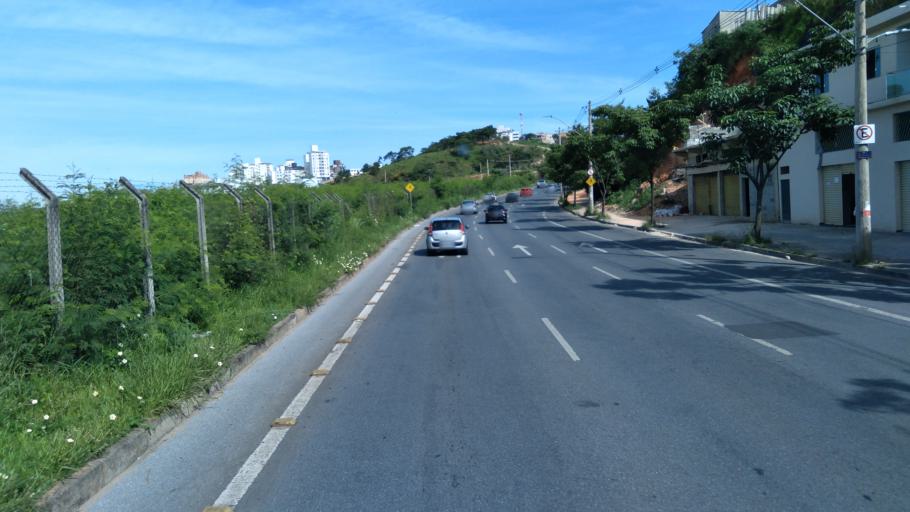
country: BR
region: Minas Gerais
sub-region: Belo Horizonte
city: Belo Horizonte
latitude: -19.9009
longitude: -43.9914
